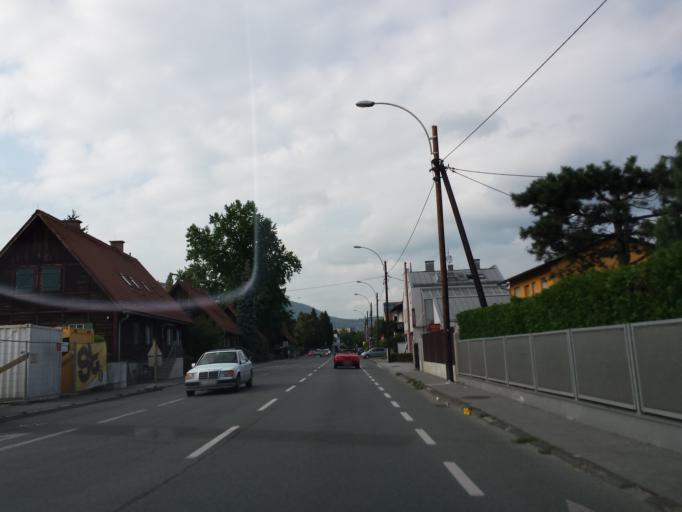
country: AT
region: Styria
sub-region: Graz Stadt
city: Wetzelsdorf
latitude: 47.0479
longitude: 15.3949
